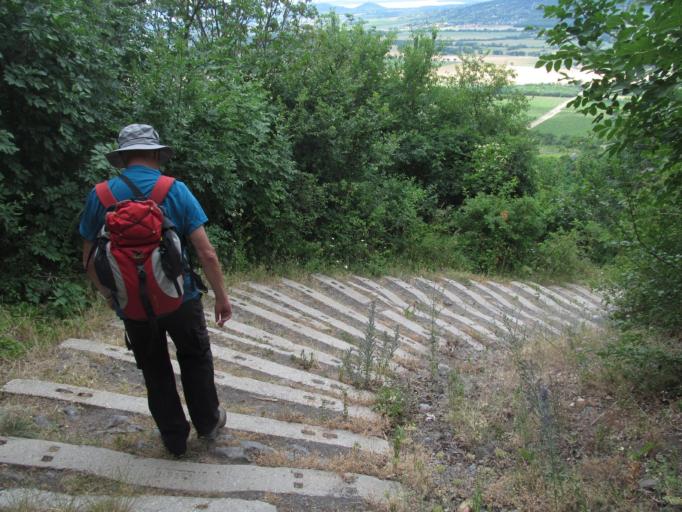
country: HU
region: Veszprem
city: Tapolca
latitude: 46.8707
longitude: 17.5024
